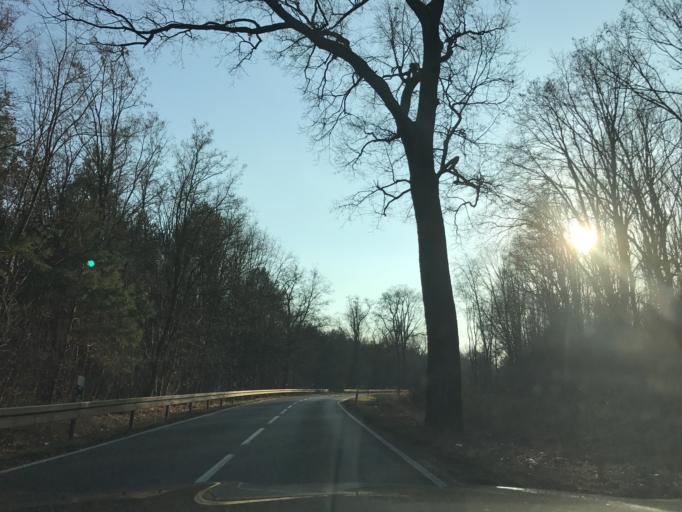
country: DE
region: Brandenburg
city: Brandenburg an der Havel
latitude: 52.3683
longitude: 12.5037
